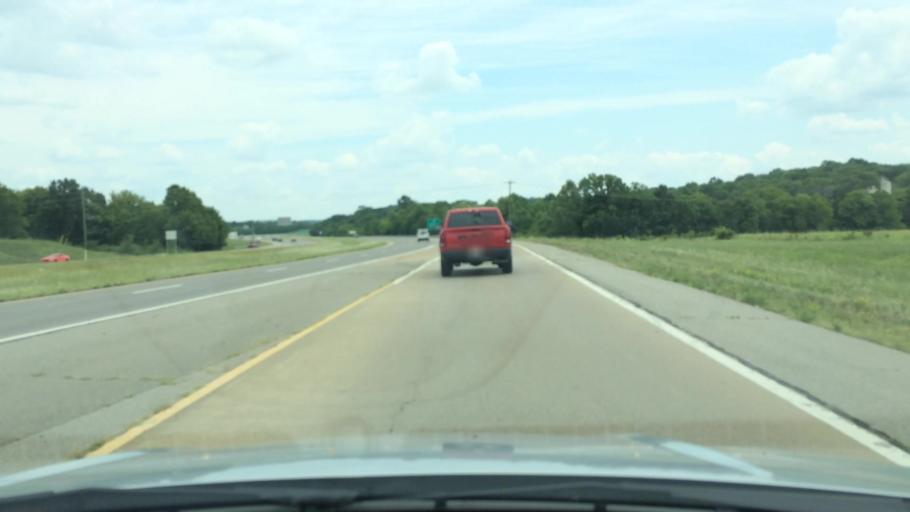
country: US
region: Tennessee
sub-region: Maury County
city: Spring Hill
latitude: 35.7346
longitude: -86.8893
